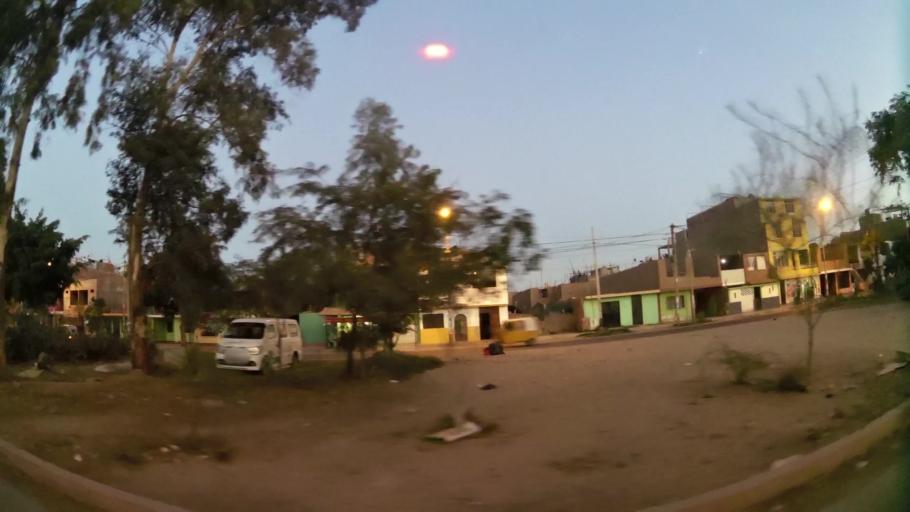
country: PE
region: Ica
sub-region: Provincia de Ica
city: Ica
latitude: -14.0794
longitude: -75.7344
